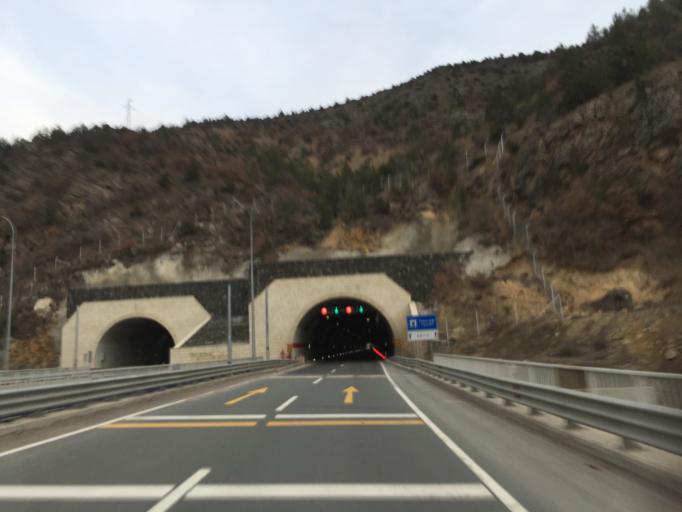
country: TR
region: Gumushane
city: Gumushkhane
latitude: 40.5181
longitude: 39.4111
